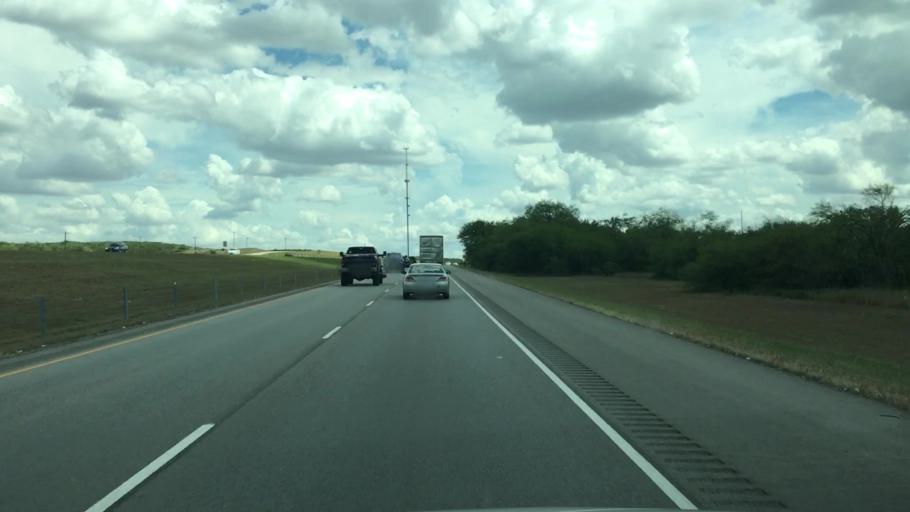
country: US
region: Texas
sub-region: San Patricio County
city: Mathis
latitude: 28.2595
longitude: -97.9279
